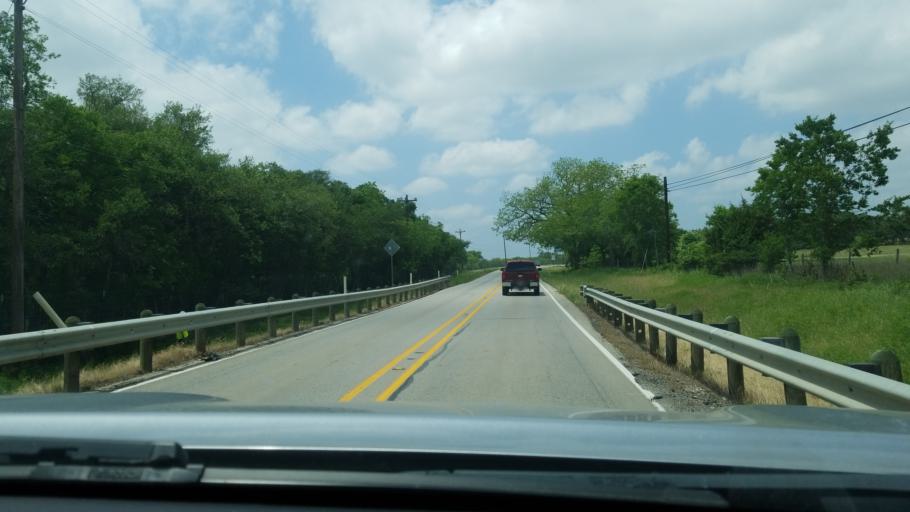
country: US
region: Texas
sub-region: Hays County
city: Dripping Springs
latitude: 30.1597
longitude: -98.0758
